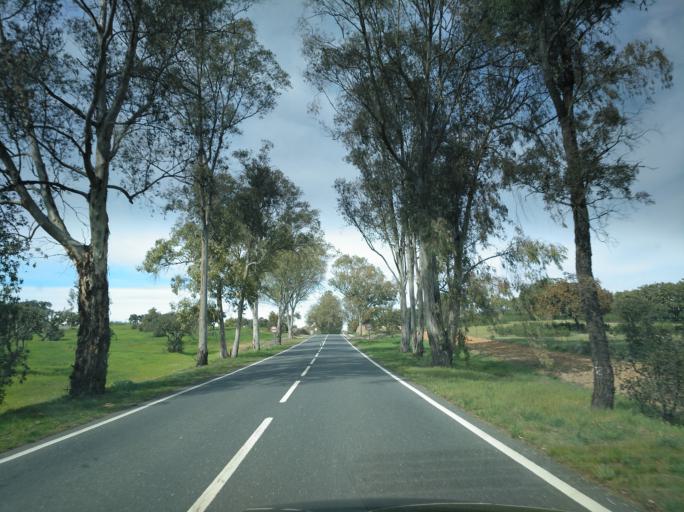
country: PT
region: Beja
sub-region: Mertola
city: Mertola
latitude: 37.7258
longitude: -7.7644
